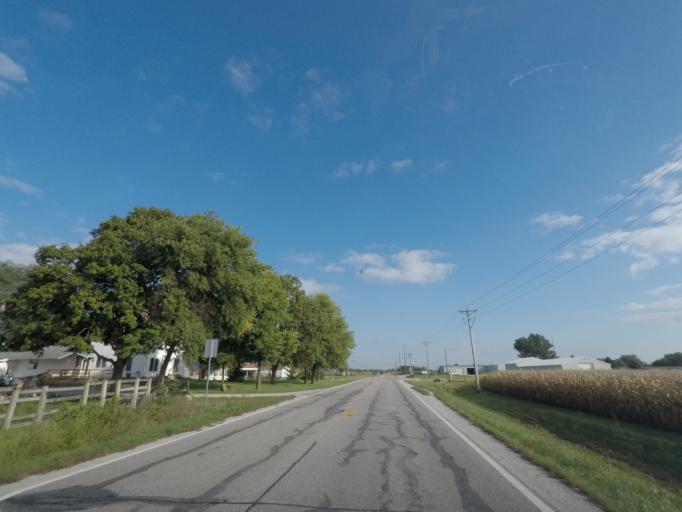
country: US
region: Iowa
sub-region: Story County
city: Nevada
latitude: 42.0002
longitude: -93.4628
